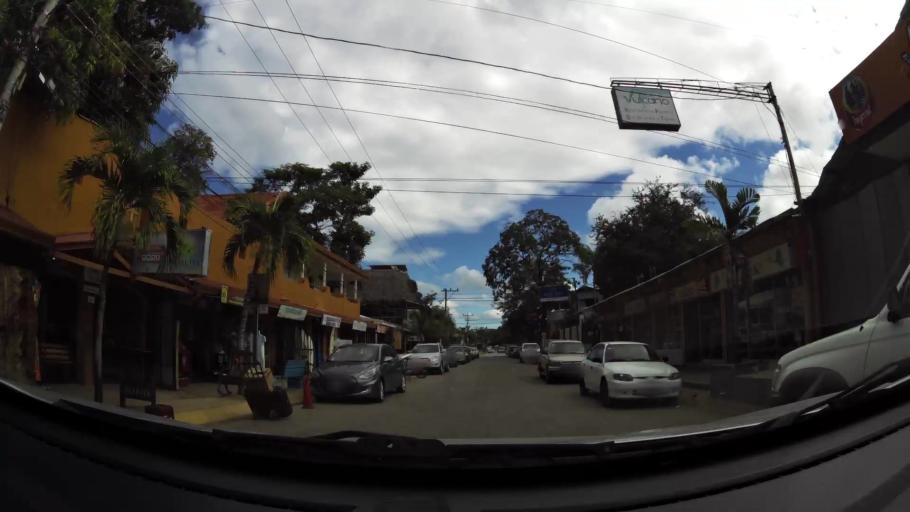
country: CR
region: Guanacaste
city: Santa Cruz
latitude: 10.2989
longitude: -85.8421
